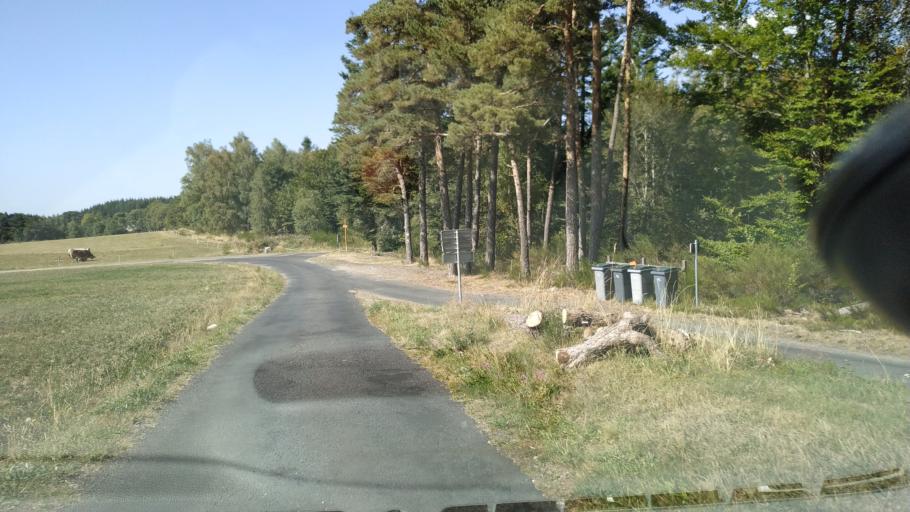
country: FR
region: Rhone-Alpes
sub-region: Departement de l'Ardeche
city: Saint-Agreve
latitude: 45.0360
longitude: 4.4438
